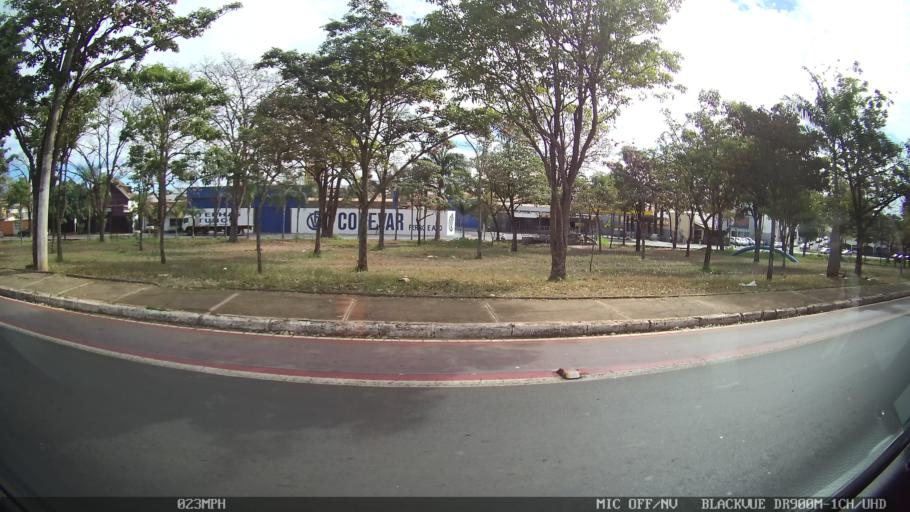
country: BR
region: Sao Paulo
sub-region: Catanduva
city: Catanduva
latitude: -21.1456
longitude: -48.9730
